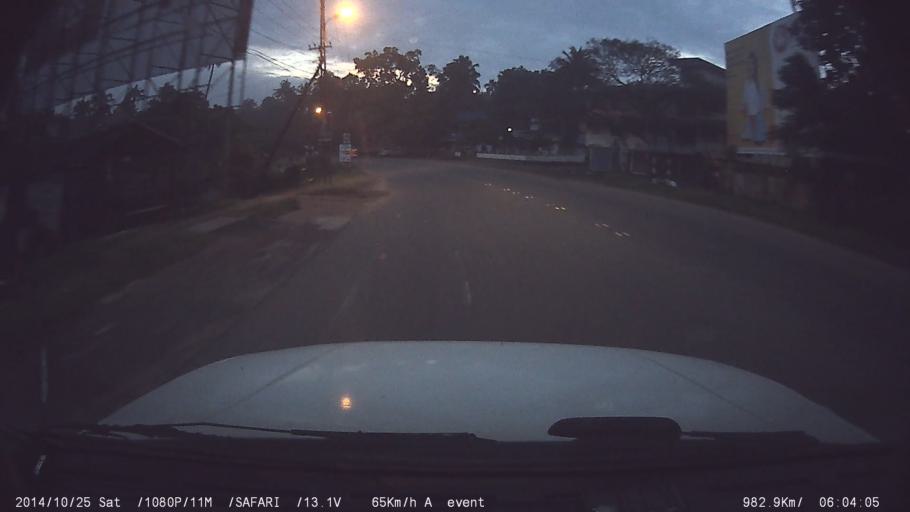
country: IN
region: Kerala
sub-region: Ernakulam
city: Angamali
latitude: 10.1854
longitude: 76.3982
